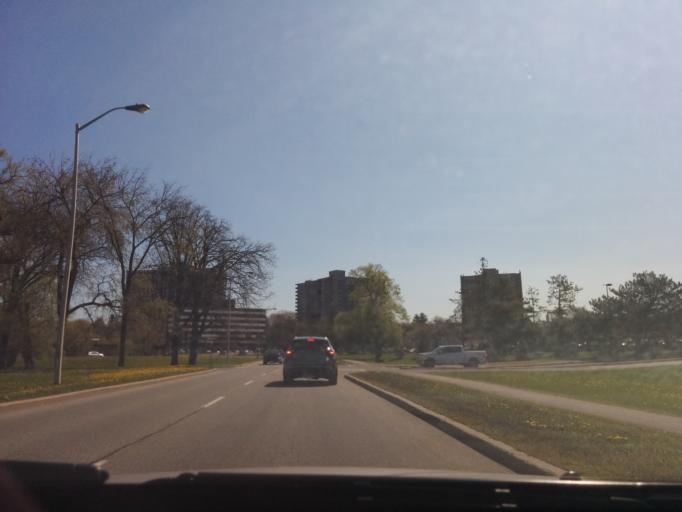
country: CA
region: Ontario
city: Ottawa
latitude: 45.3867
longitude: -75.6799
